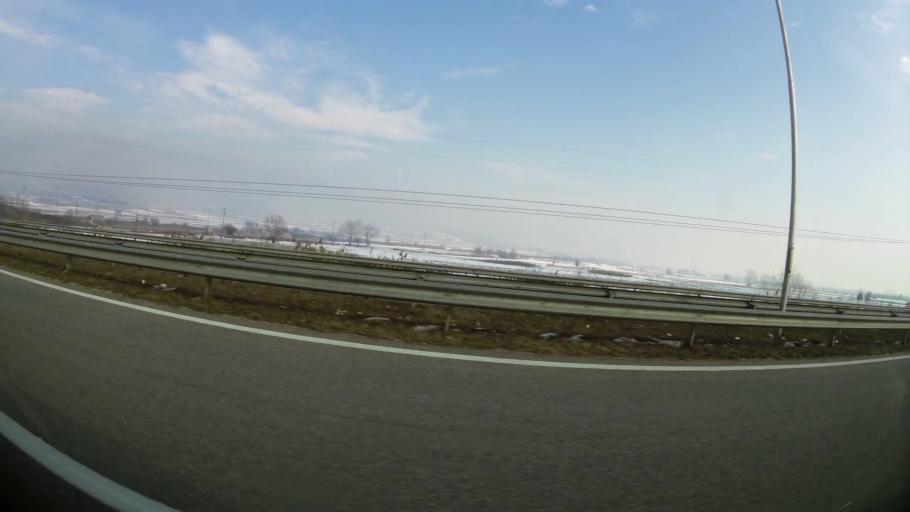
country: MK
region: Aracinovo
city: Arachinovo
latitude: 42.0257
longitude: 21.5308
